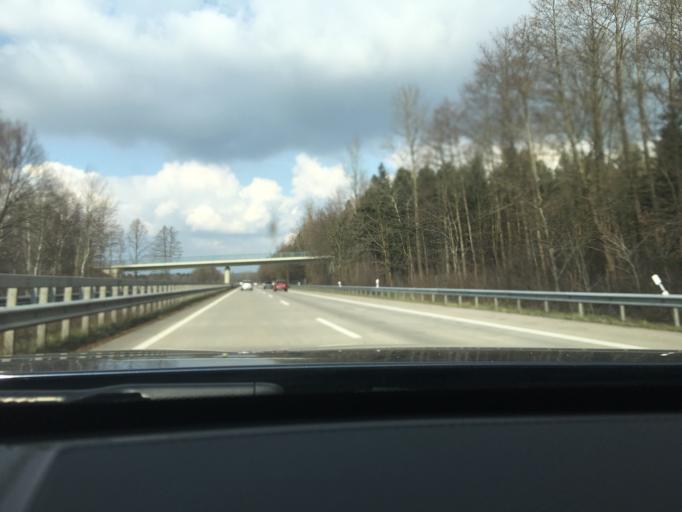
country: DE
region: Lower Saxony
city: Schwanewede
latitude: 53.2607
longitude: 8.6357
